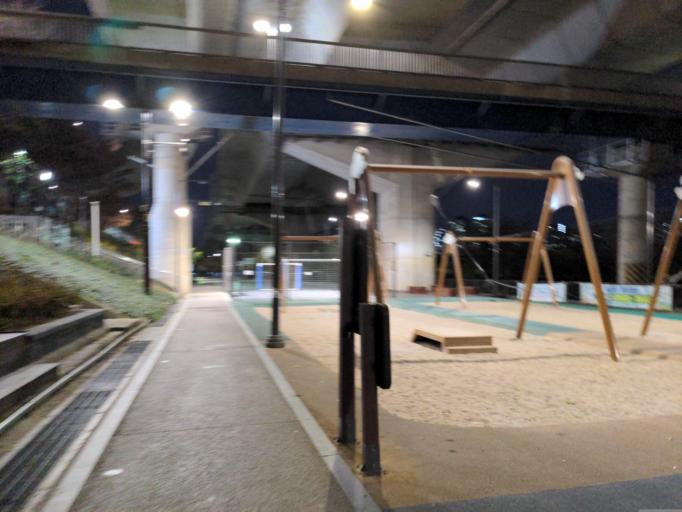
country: KR
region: Seoul
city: Seoul
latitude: 37.5620
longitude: 127.0493
